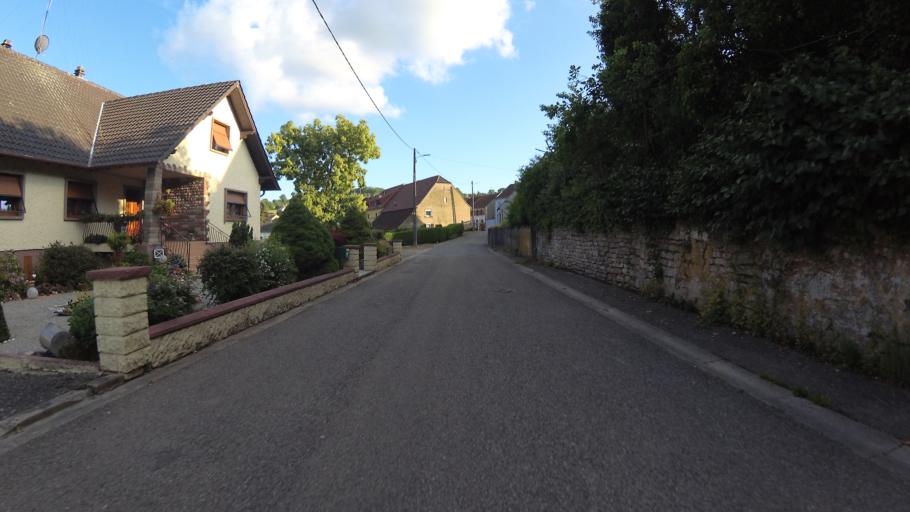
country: FR
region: Alsace
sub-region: Departement du Bas-Rhin
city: Oermingen
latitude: 48.9985
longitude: 7.1293
